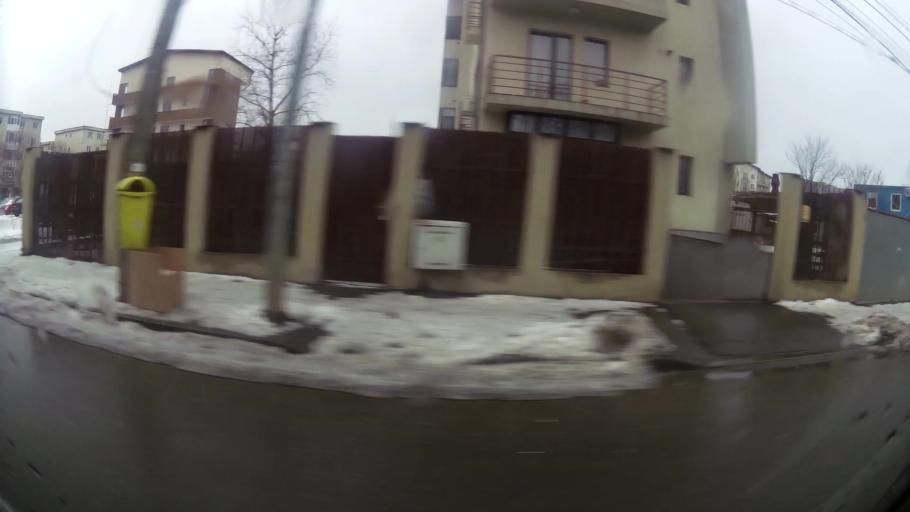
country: RO
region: Ilfov
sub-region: Comuna Chiajna
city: Rosu
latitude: 44.4301
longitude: 26.0128
